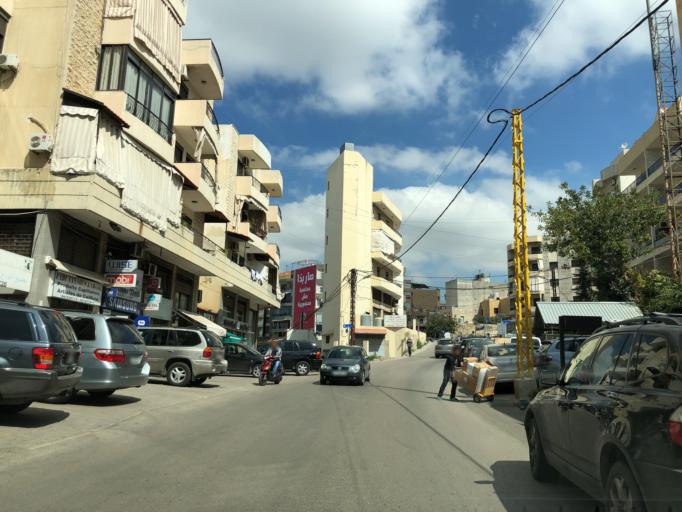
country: LB
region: Mont-Liban
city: Jdaidet el Matn
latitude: 33.8552
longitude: 35.5746
